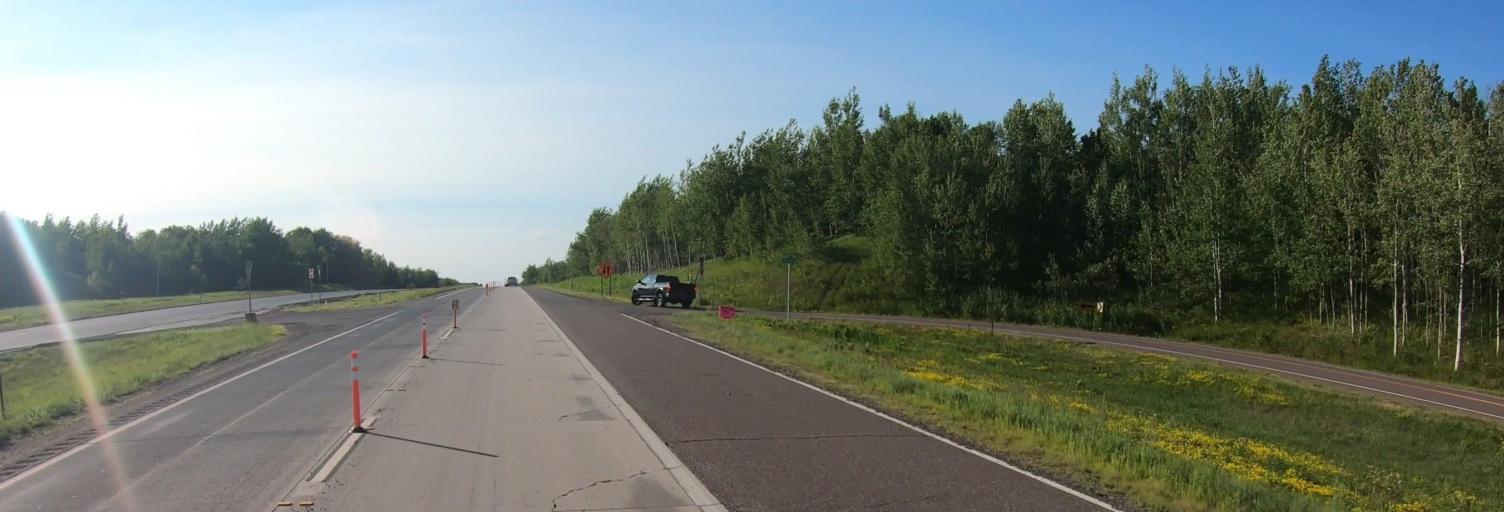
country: US
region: Minnesota
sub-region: Saint Louis County
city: Hermantown
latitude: 46.9009
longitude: -92.3747
